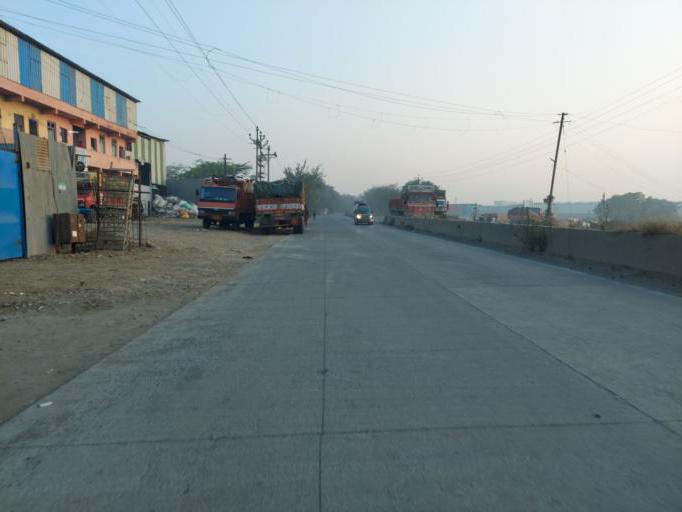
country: IN
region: Maharashtra
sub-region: Pune Division
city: Pune
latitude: 18.4643
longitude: 73.9528
